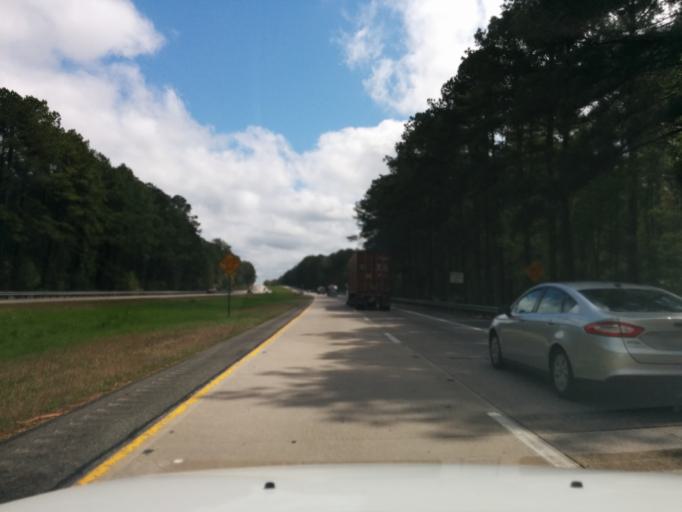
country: US
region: Georgia
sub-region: Chatham County
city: Bloomingdale
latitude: 32.1472
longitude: -81.4209
